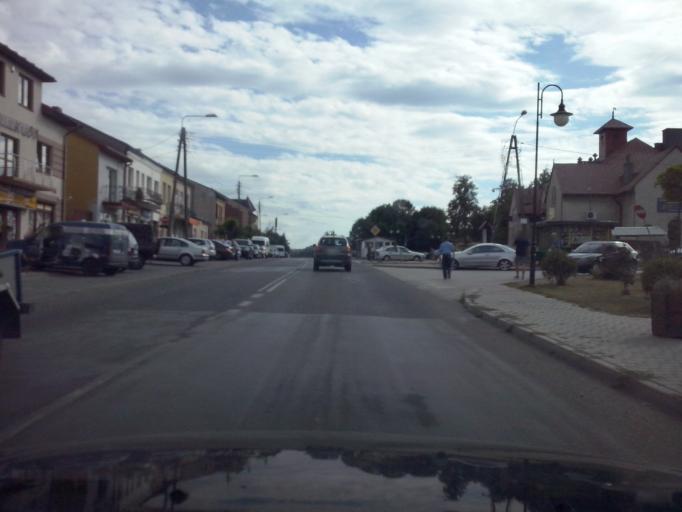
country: PL
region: Swietokrzyskie
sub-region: Powiat kielecki
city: Lagow
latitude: 50.7749
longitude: 21.0841
